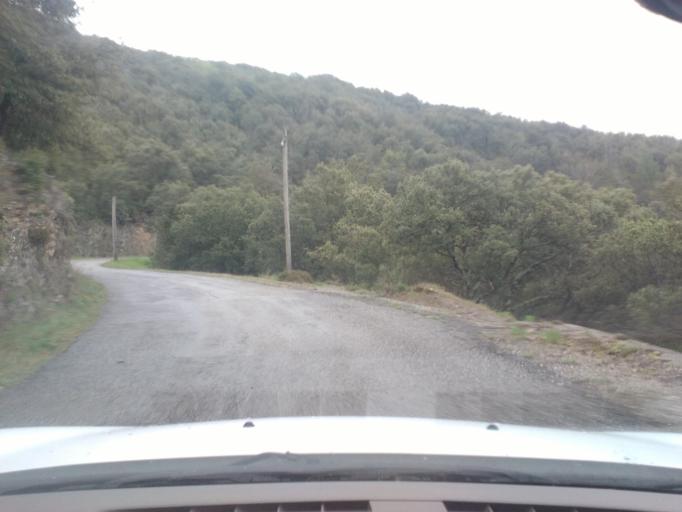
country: FR
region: Languedoc-Roussillon
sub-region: Departement du Gard
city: Sumene
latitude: 44.0324
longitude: 3.6926
